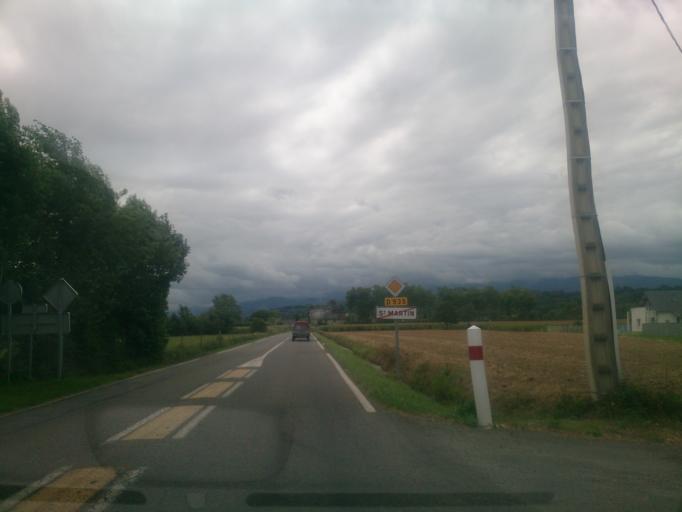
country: FR
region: Midi-Pyrenees
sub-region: Departement des Hautes-Pyrenees
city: Horgues
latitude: 43.1581
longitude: 0.0877
